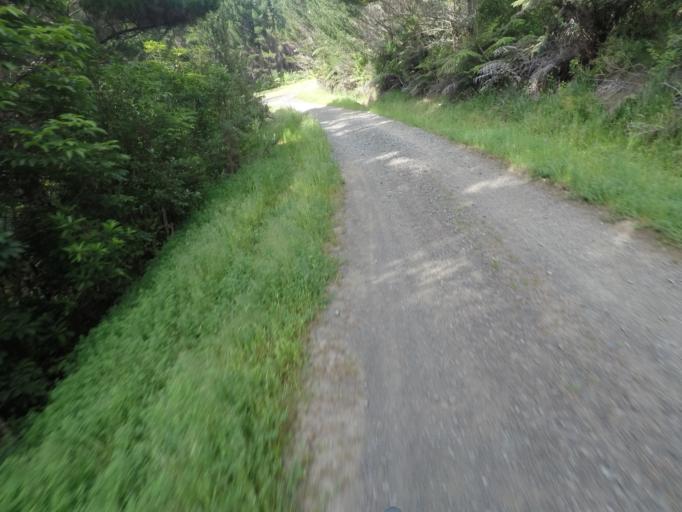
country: NZ
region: Auckland
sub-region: Auckland
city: Muriwai Beach
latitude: -36.7473
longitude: 174.5633
